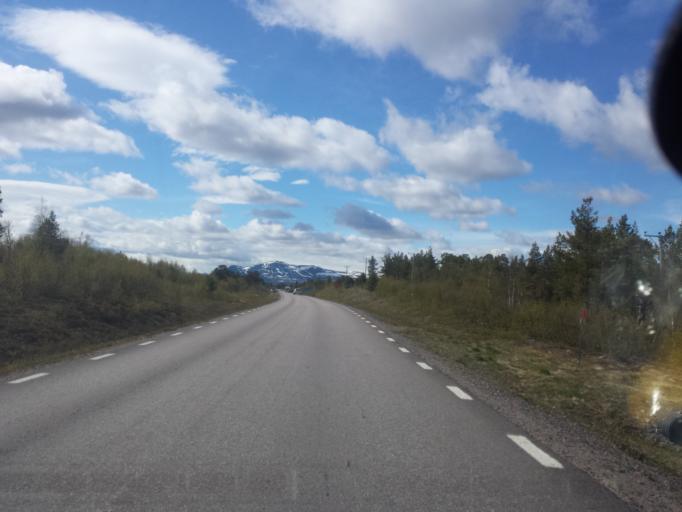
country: SE
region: Norrbotten
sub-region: Kiruna Kommun
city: Kiruna
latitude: 67.9891
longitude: 19.9303
